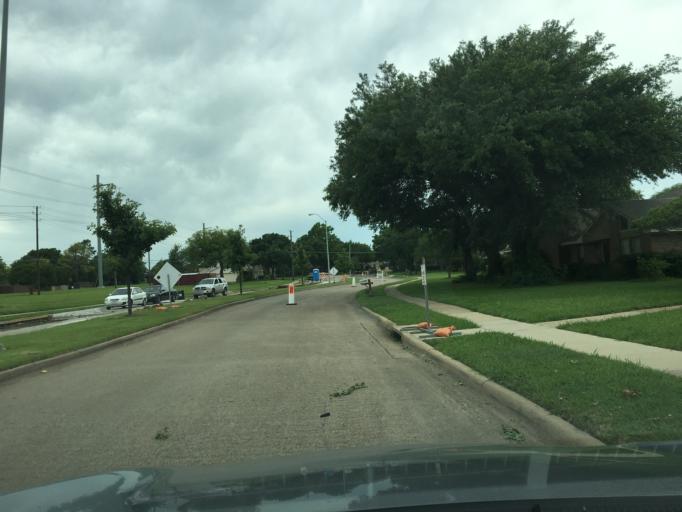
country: US
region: Texas
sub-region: Dallas County
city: Richardson
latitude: 32.9387
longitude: -96.7084
